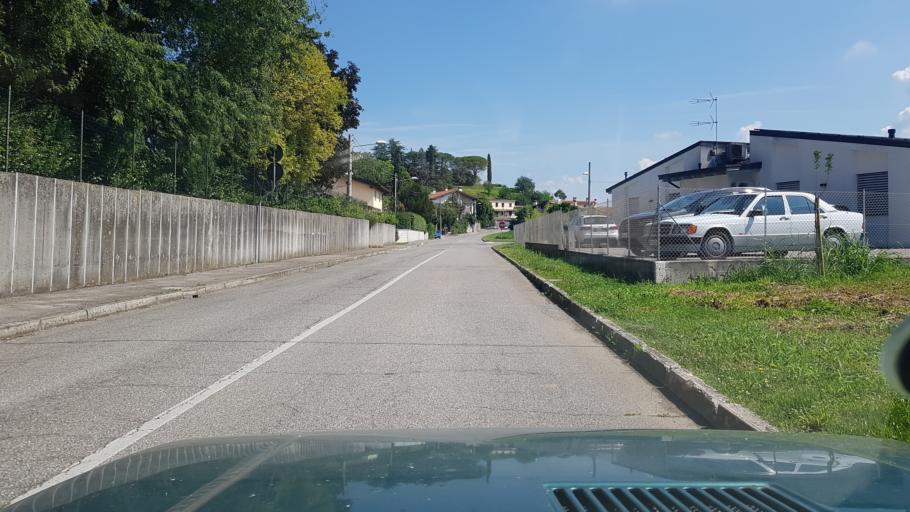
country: IT
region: Friuli Venezia Giulia
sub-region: Provincia di Gorizia
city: Mossa
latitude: 45.9363
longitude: 13.5418
